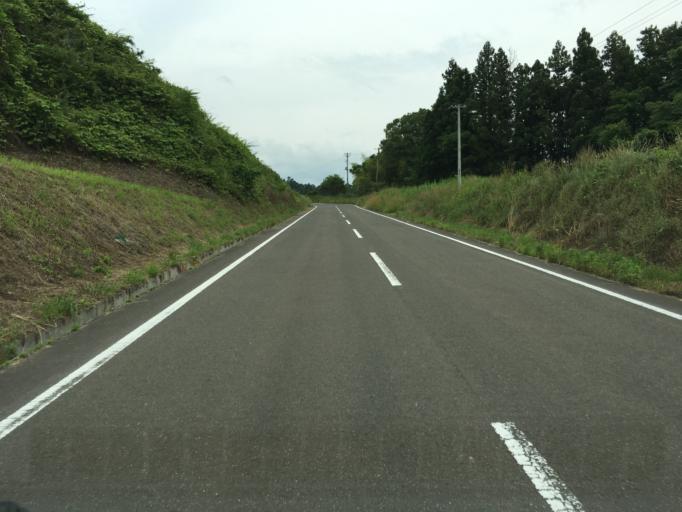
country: JP
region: Fukushima
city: Nihommatsu
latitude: 37.6304
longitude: 140.5356
